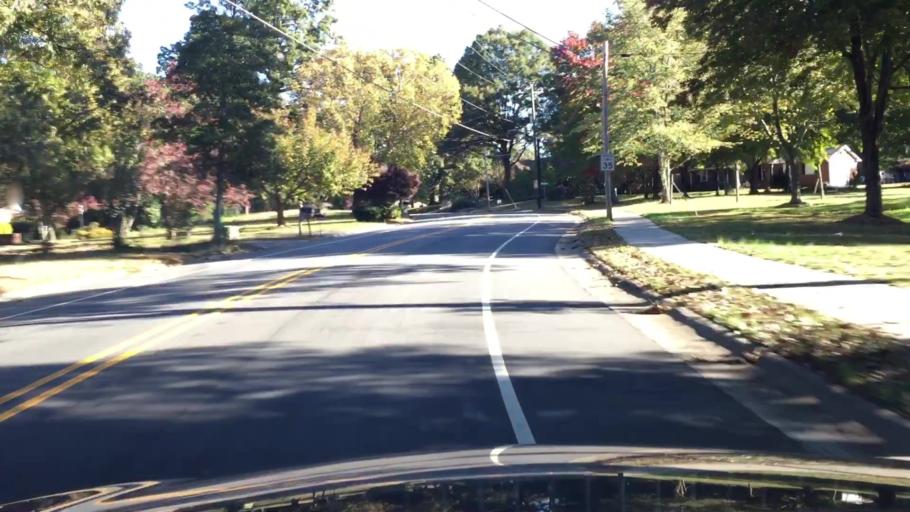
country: US
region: North Carolina
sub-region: Iredell County
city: Mooresville
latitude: 35.5683
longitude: -80.8023
